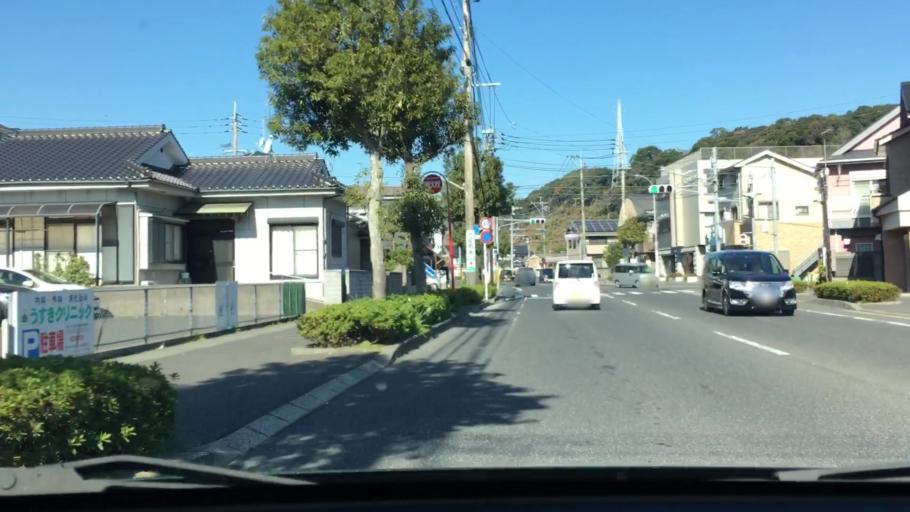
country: JP
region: Kagoshima
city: Kagoshima-shi
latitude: 31.5472
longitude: 130.5333
